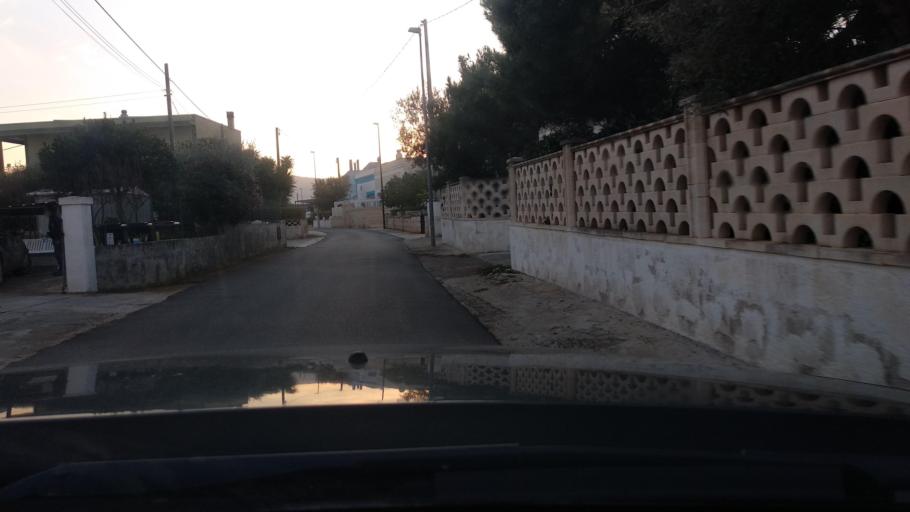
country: IT
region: Apulia
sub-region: Provincia di Brindisi
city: Fasano
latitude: 40.8834
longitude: 17.3350
